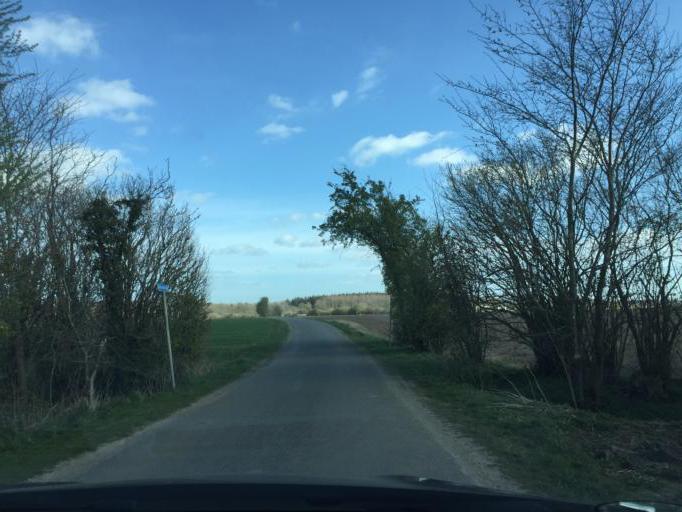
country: DK
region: South Denmark
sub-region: Kerteminde Kommune
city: Langeskov
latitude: 55.3066
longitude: 10.5434
